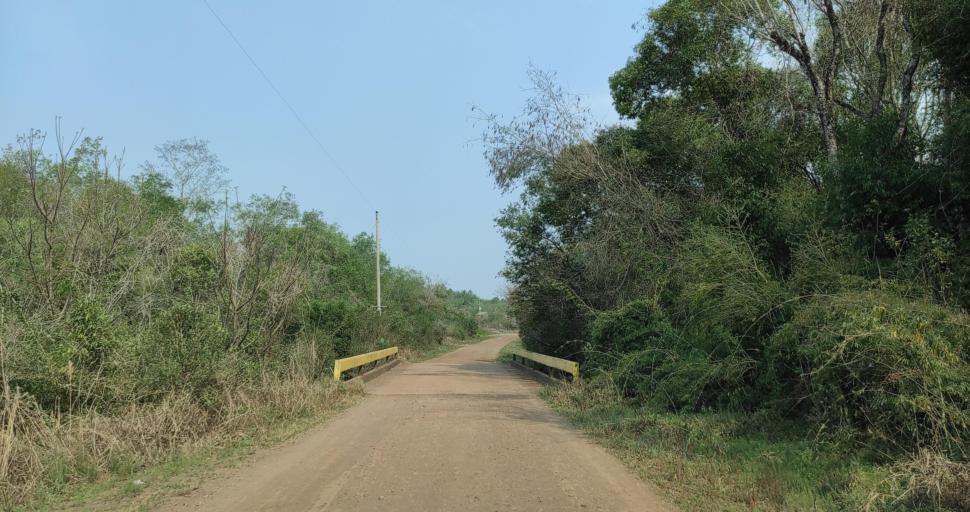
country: AR
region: Misiones
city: Cerro Cora
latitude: -27.5672
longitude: -55.5843
